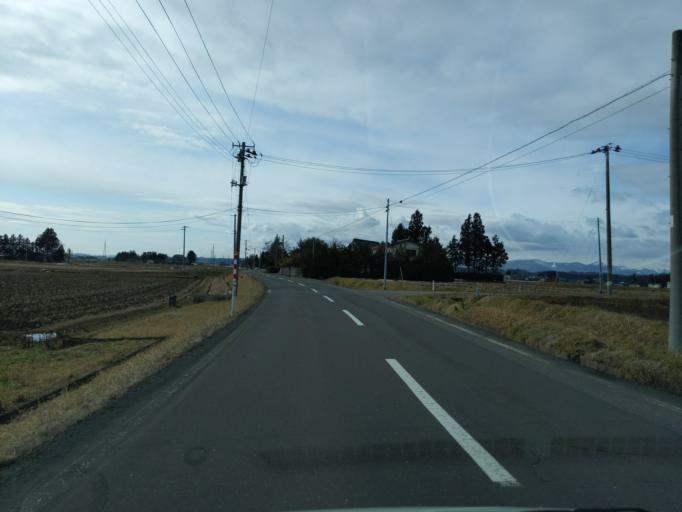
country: JP
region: Iwate
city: Mizusawa
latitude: 39.0903
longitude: 141.1674
